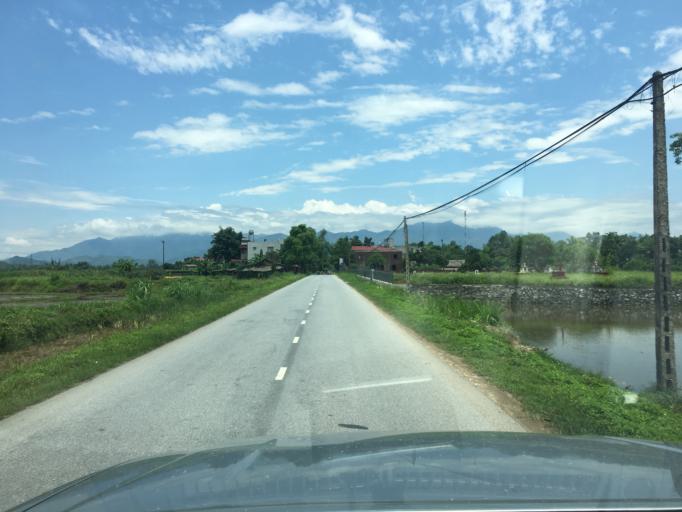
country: VN
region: Yen Bai
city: Son Thinh
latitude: 21.6366
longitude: 104.5031
